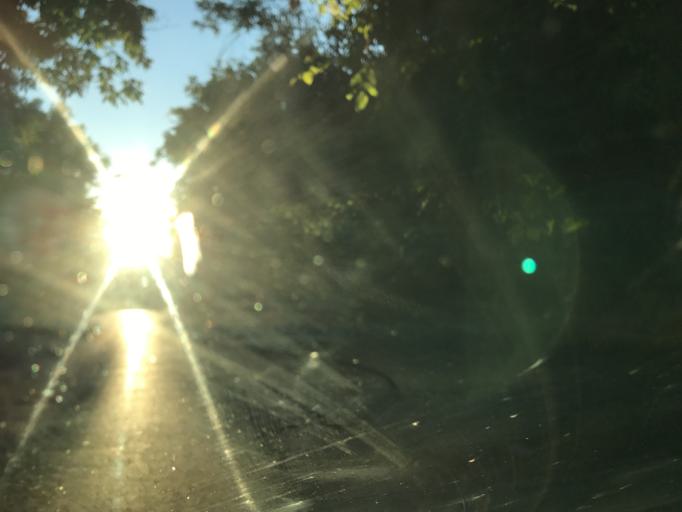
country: BG
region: Vidin
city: Bregovo
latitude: 44.1204
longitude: 22.5873
